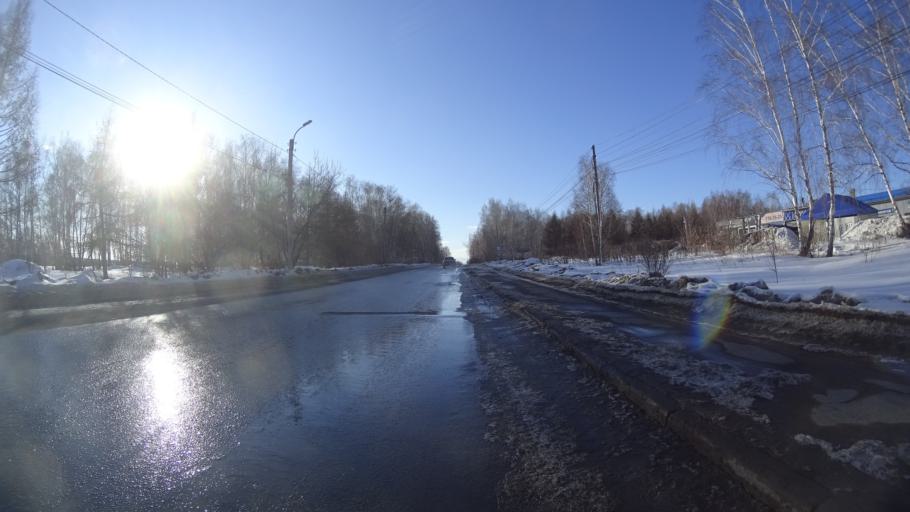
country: RU
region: Chelyabinsk
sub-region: Gorod Chelyabinsk
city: Chelyabinsk
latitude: 55.1489
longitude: 61.2938
